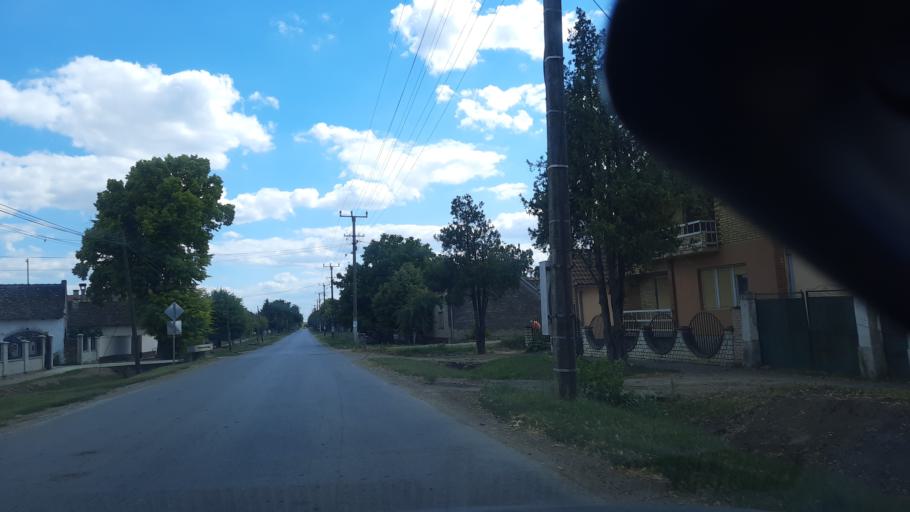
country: RS
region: Autonomna Pokrajina Vojvodina
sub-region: Sremski Okrug
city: Pecinci
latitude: 44.9337
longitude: 20.0071
